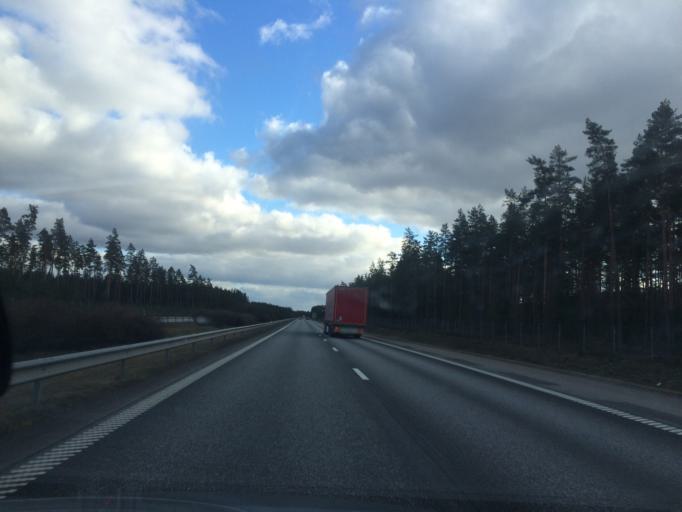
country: SE
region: Joenkoeping
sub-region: Vaggeryds Kommun
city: Skillingaryd
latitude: 57.3733
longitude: 14.1012
